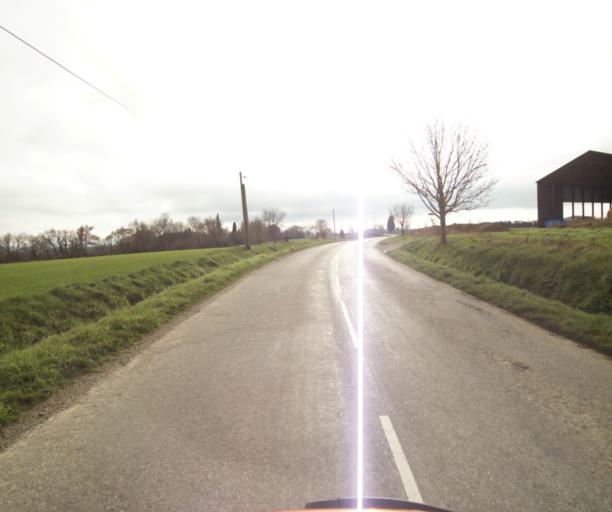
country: FR
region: Languedoc-Roussillon
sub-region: Departement de l'Aude
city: Belpech
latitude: 43.1961
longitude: 1.7316
